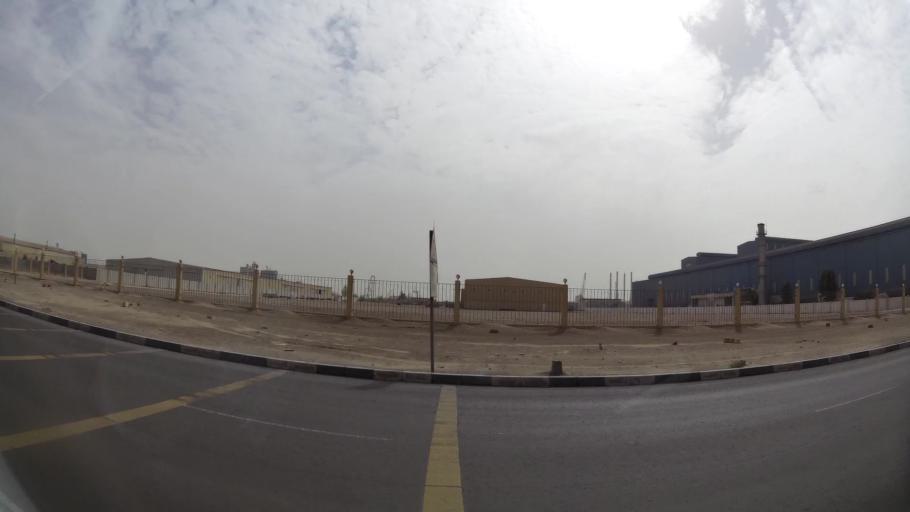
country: AE
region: Abu Dhabi
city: Abu Dhabi
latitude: 24.3226
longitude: 54.4829
